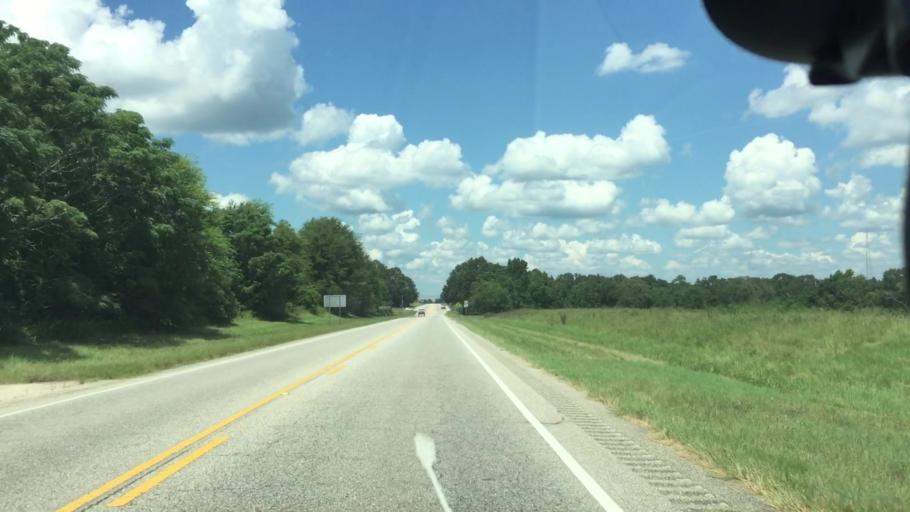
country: US
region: Alabama
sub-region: Coffee County
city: New Brockton
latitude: 31.4215
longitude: -85.8867
